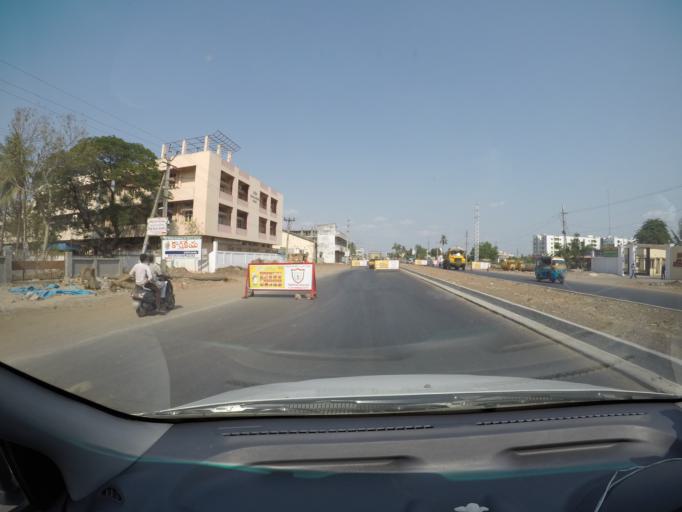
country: IN
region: Andhra Pradesh
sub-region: Krishna
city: Yanamalakuduru
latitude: 16.4734
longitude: 80.7149
